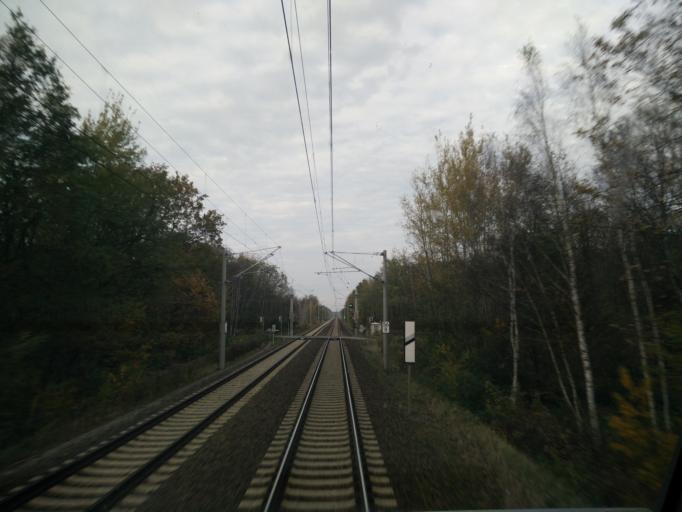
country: DE
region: Brandenburg
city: Halbe
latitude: 52.0554
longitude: 13.7220
